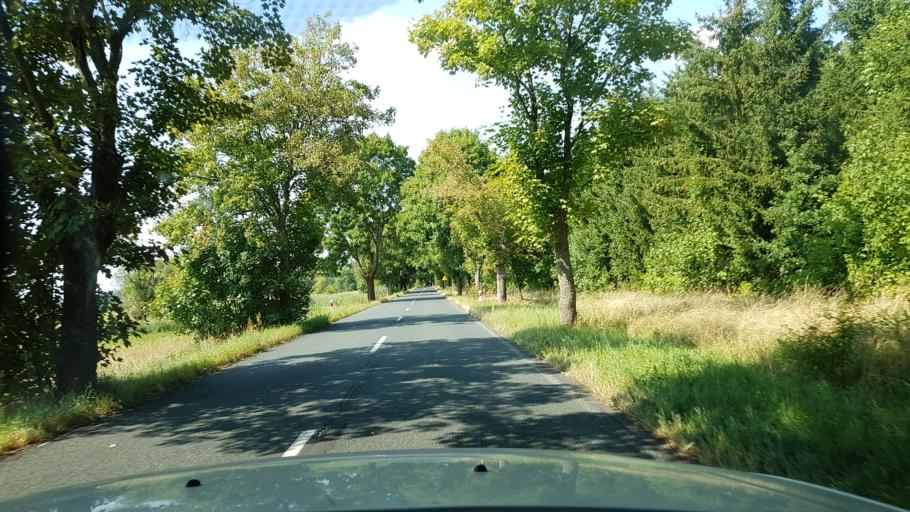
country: PL
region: West Pomeranian Voivodeship
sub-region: Powiat gryfinski
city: Cedynia
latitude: 52.8303
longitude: 14.2152
